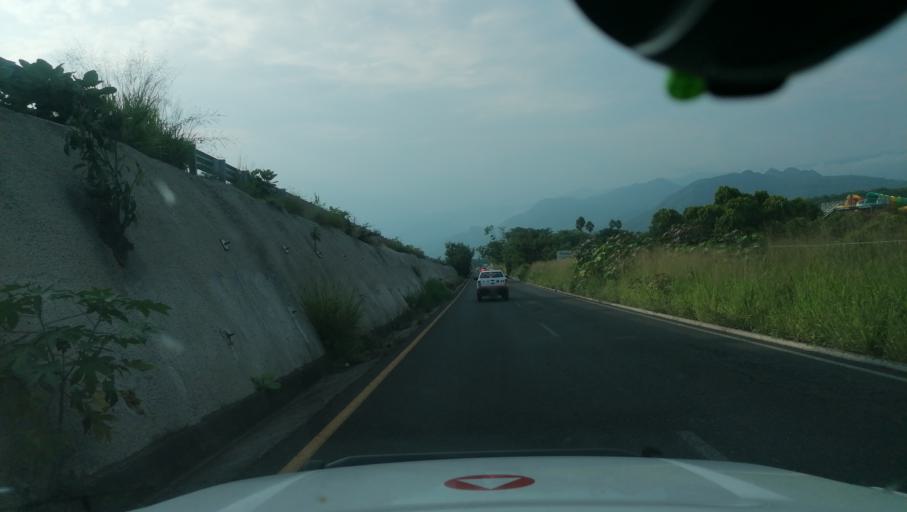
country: MX
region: Morelos
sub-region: Yautepec
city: Cocoyoc
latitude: 18.8936
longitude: -98.9753
